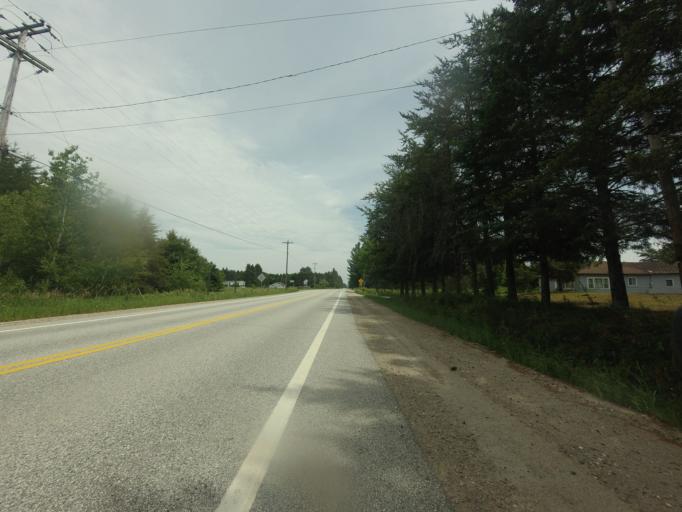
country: CA
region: Quebec
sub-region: Outaouais
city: Wakefield
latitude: 45.9512
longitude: -76.0581
